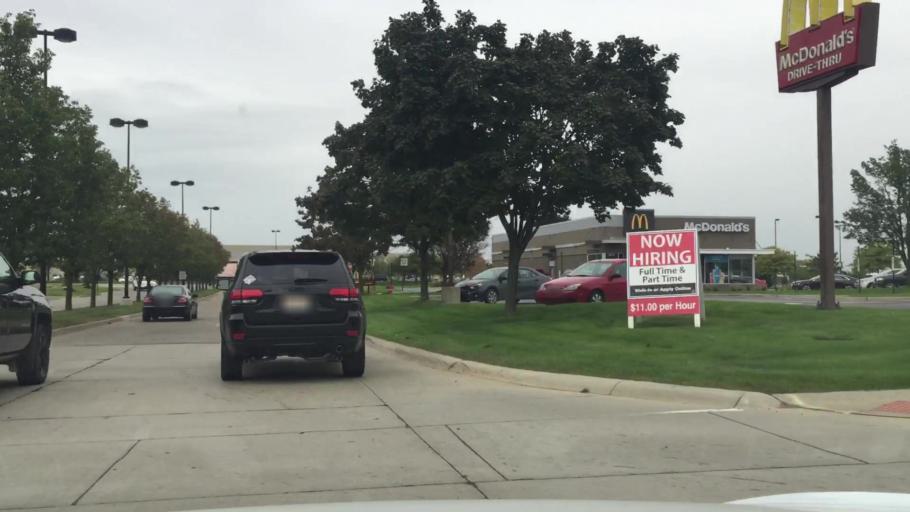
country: US
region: Michigan
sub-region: Oakland County
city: Pontiac
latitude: 42.7018
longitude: -83.3066
